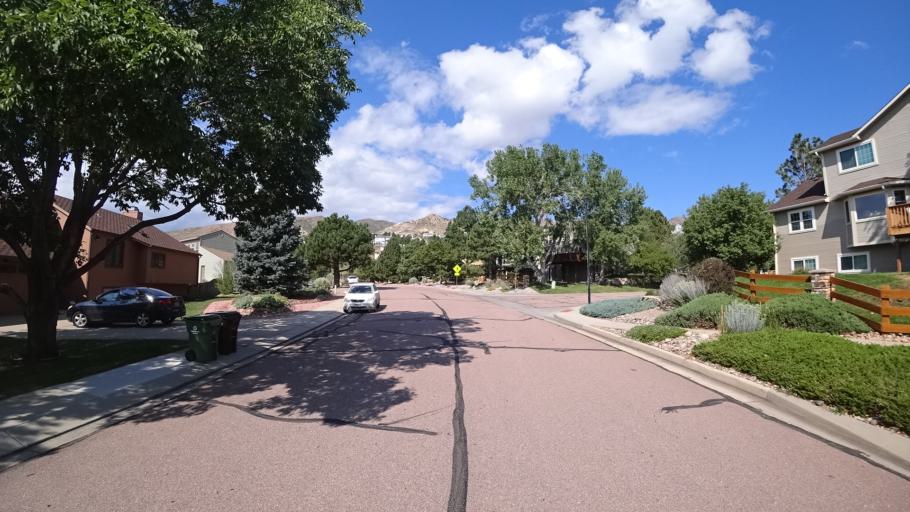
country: US
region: Colorado
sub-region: El Paso County
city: Manitou Springs
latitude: 38.9095
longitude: -104.8723
